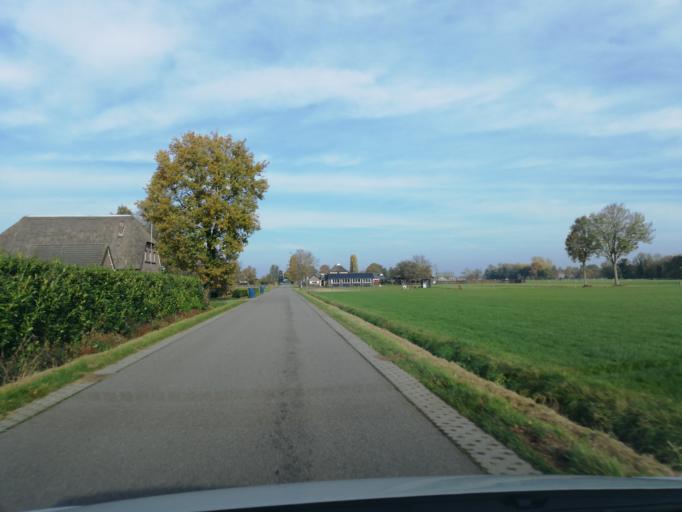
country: NL
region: Gelderland
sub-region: Gemeente Epe
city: Vaassen
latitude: 52.2514
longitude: 6.0159
